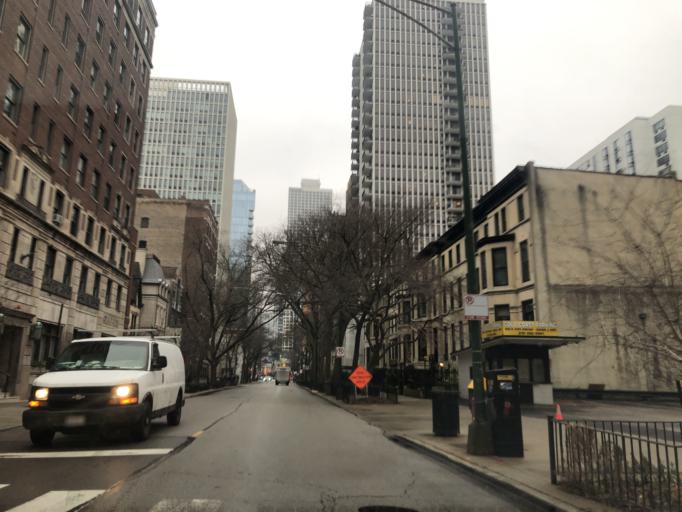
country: US
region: Illinois
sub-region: Cook County
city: Chicago
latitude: 41.9059
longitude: -87.6287
